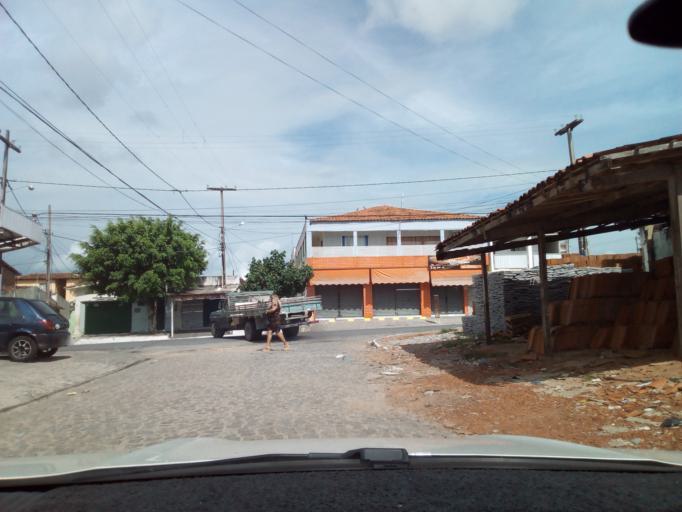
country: BR
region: Paraiba
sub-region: Joao Pessoa
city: Joao Pessoa
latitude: -7.1811
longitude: -34.8472
